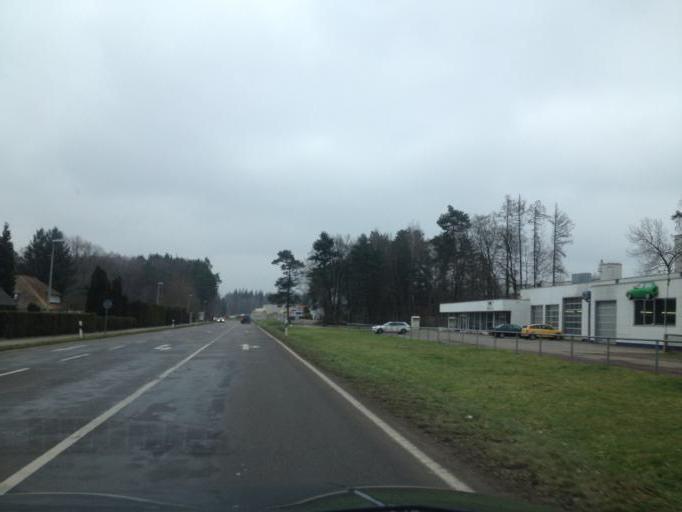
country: DE
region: Rheinland-Pfalz
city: Waldmohr
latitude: 49.3848
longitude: 7.3497
